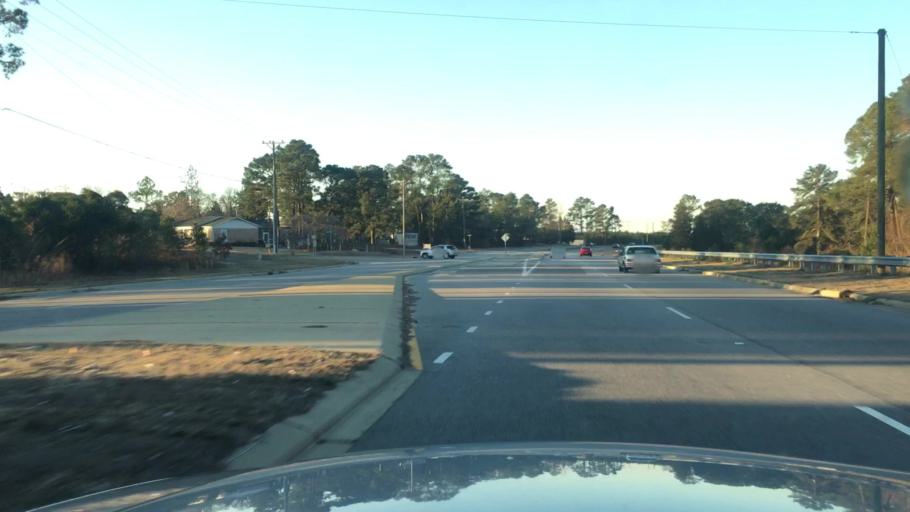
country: US
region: North Carolina
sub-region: Cumberland County
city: Hope Mills
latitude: 34.9951
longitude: -78.9425
